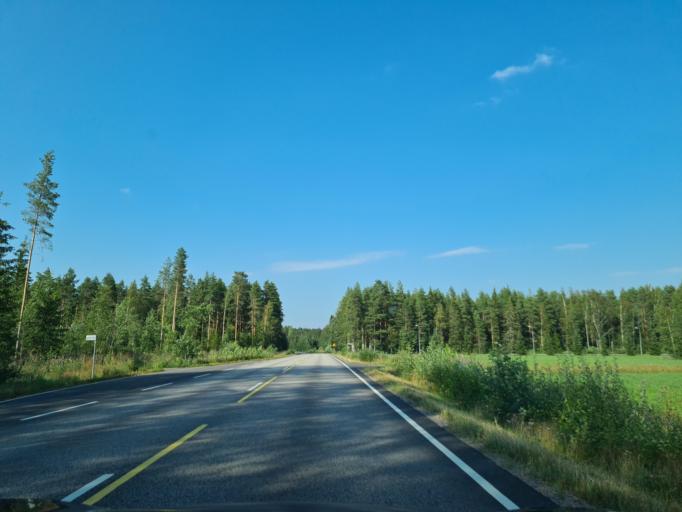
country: FI
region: Satakunta
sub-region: Pohjois-Satakunta
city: Karvia
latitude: 62.2225
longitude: 22.6120
